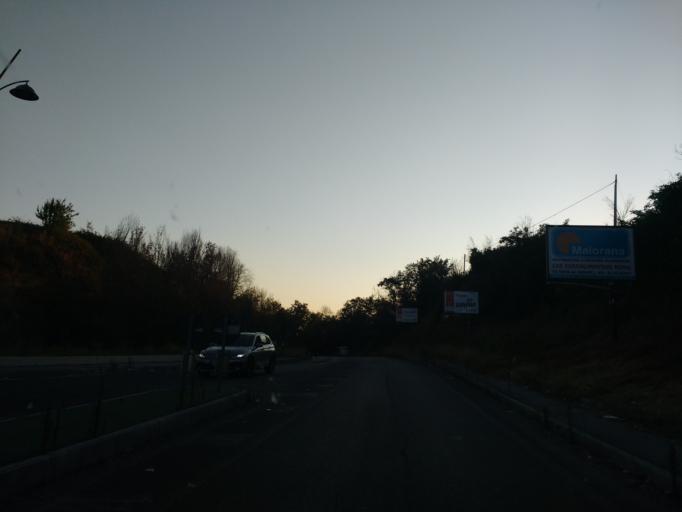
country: IT
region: Latium
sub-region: Citta metropolitana di Roma Capitale
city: Setteville
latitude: 41.9472
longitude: 12.6713
